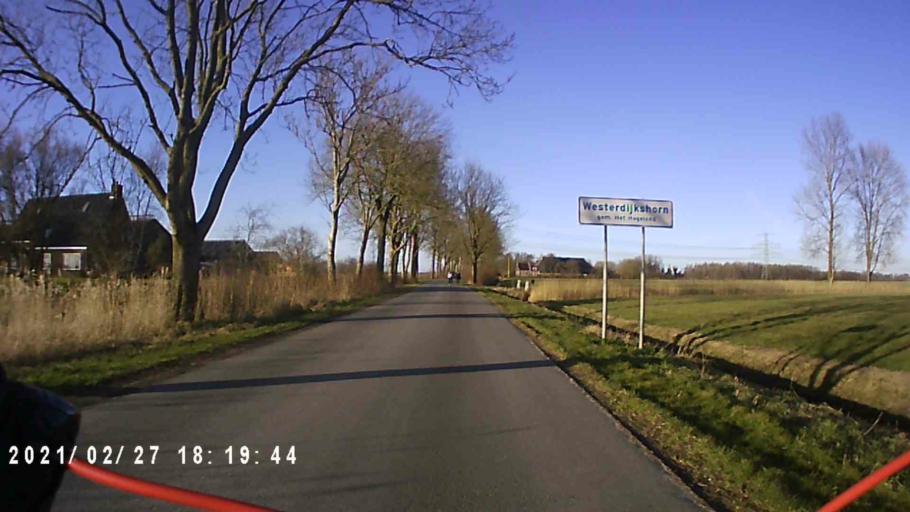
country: NL
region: Groningen
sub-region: Gemeente Bedum
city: Bedum
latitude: 53.3043
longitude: 6.5747
